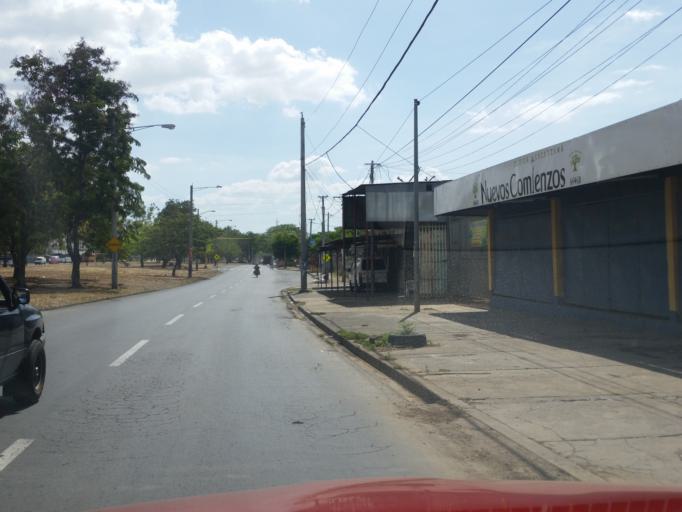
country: NI
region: Managua
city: Managua
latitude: 12.1541
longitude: -86.2648
